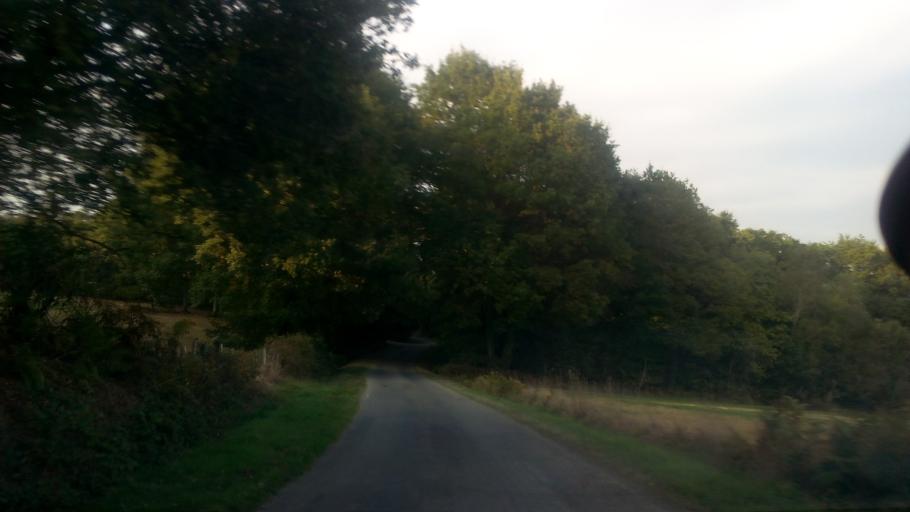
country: FR
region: Brittany
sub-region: Departement du Morbihan
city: Saint-Jean-la-Poterie
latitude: 47.6300
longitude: -2.1255
